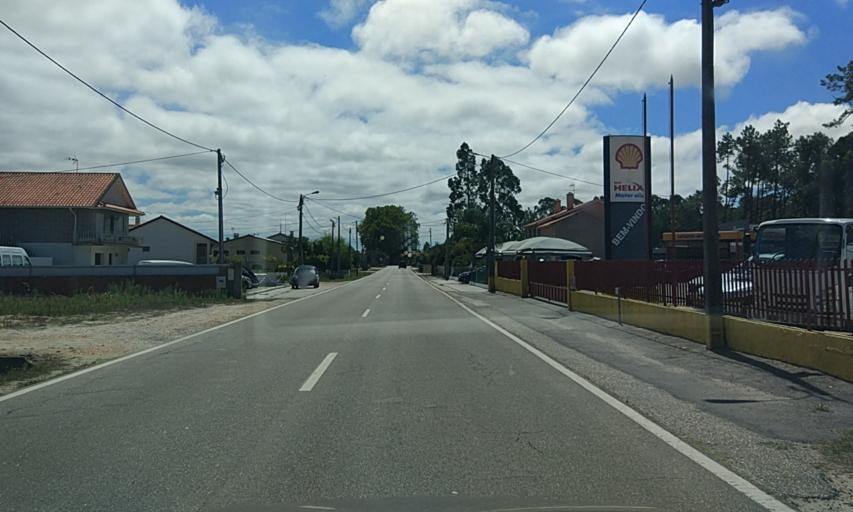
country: PT
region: Aveiro
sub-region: Vagos
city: Vagos
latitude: 40.5179
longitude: -8.6786
